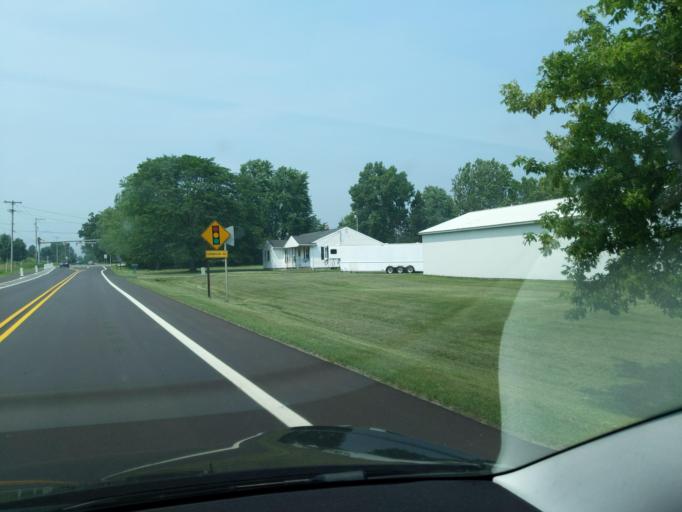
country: US
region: Michigan
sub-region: Clinton County
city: DeWitt
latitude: 42.8262
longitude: -84.5724
